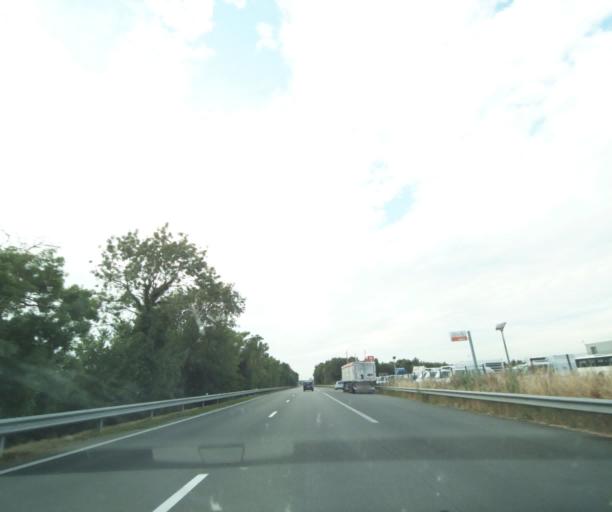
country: FR
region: Poitou-Charentes
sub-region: Departement de la Charente-Maritime
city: Chatelaillon-Plage
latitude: 46.0773
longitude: -1.0738
